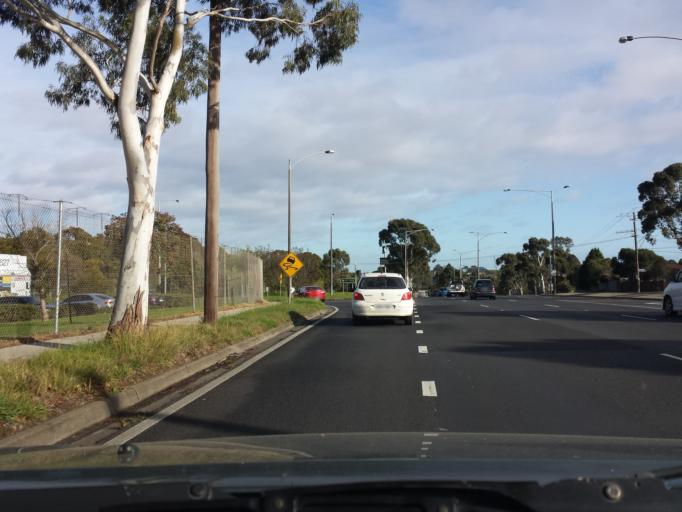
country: AU
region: Victoria
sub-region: Monash
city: Notting Hill
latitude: -37.9033
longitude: 145.1581
